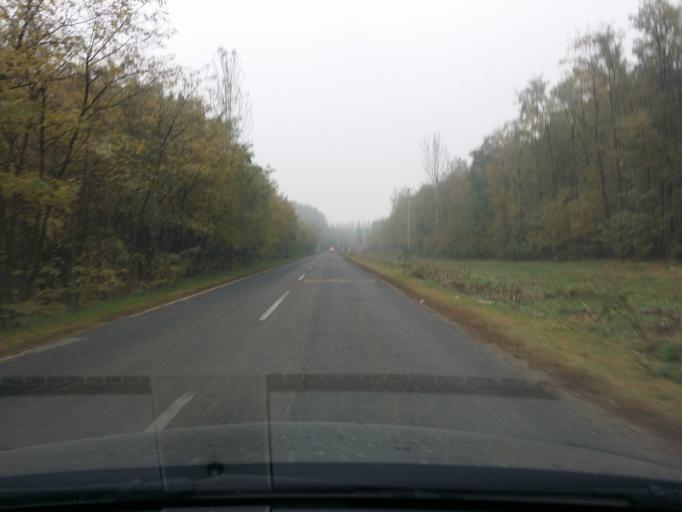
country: HU
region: Szabolcs-Szatmar-Bereg
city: Nyirbogdany
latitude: 48.0834
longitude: 21.8632
